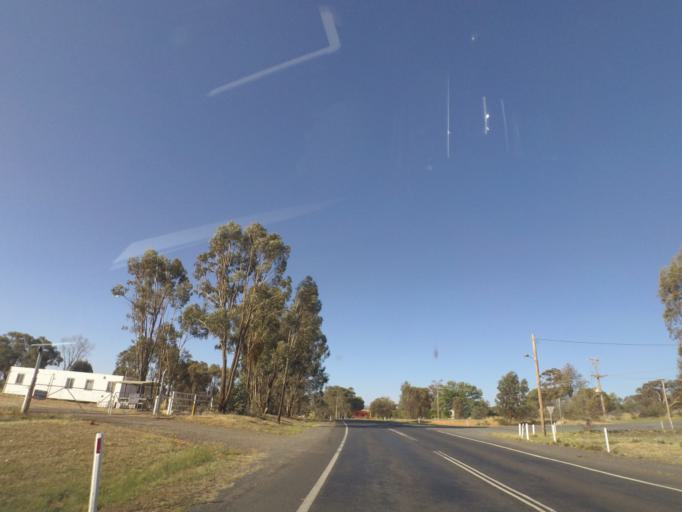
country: AU
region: New South Wales
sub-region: Wagga Wagga
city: Forest Hill
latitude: -35.2716
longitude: 147.7438
